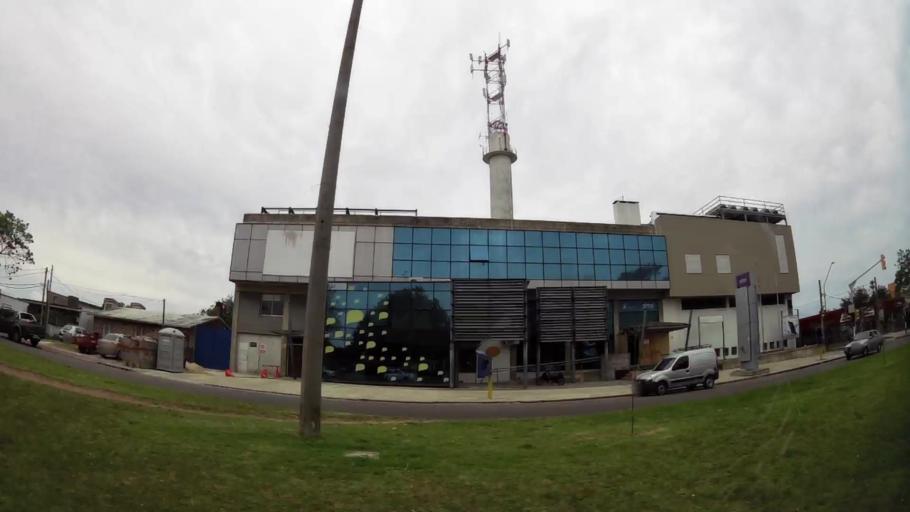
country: UY
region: Maldonado
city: Maldonado
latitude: -34.9082
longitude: -54.9632
